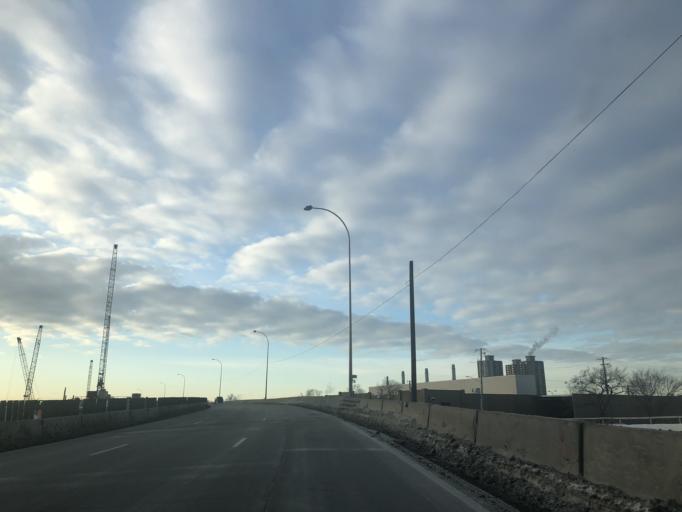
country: US
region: Minnesota
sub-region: Hennepin County
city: Minneapolis
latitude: 44.9515
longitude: -93.2756
